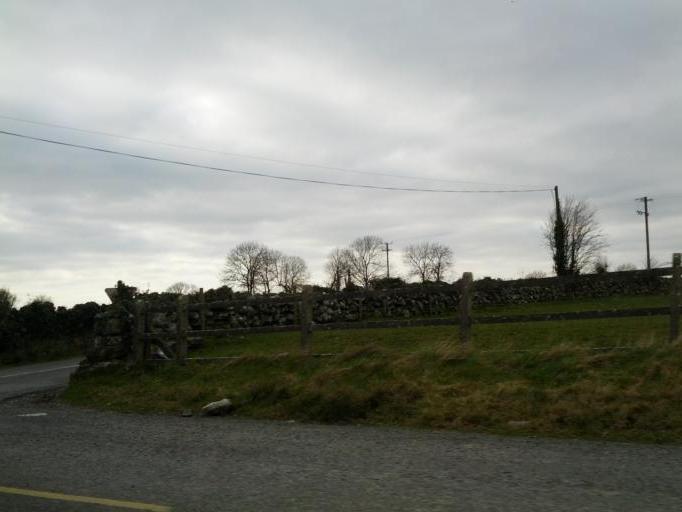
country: IE
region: Connaught
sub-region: County Galway
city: Athenry
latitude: 53.2197
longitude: -8.8085
